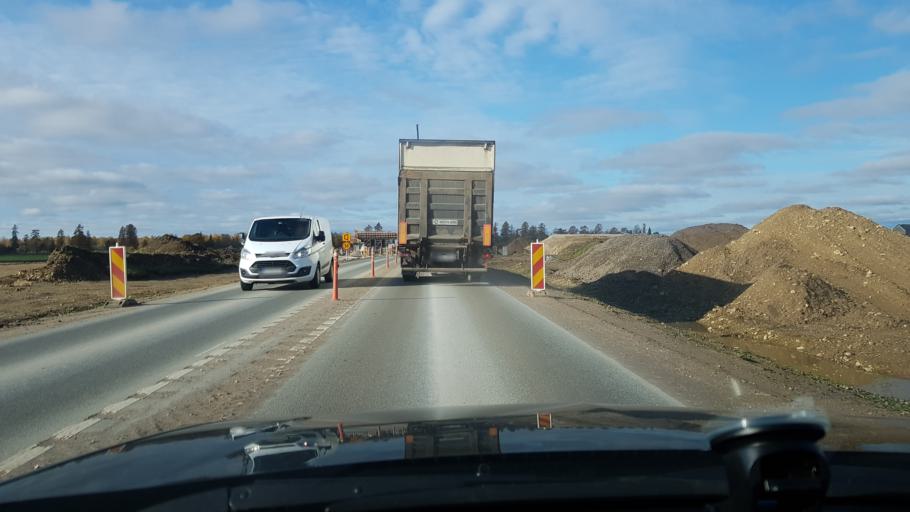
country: EE
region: Laeaene-Virumaa
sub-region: Kadrina vald
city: Kadrina
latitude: 59.4378
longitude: 26.1451
